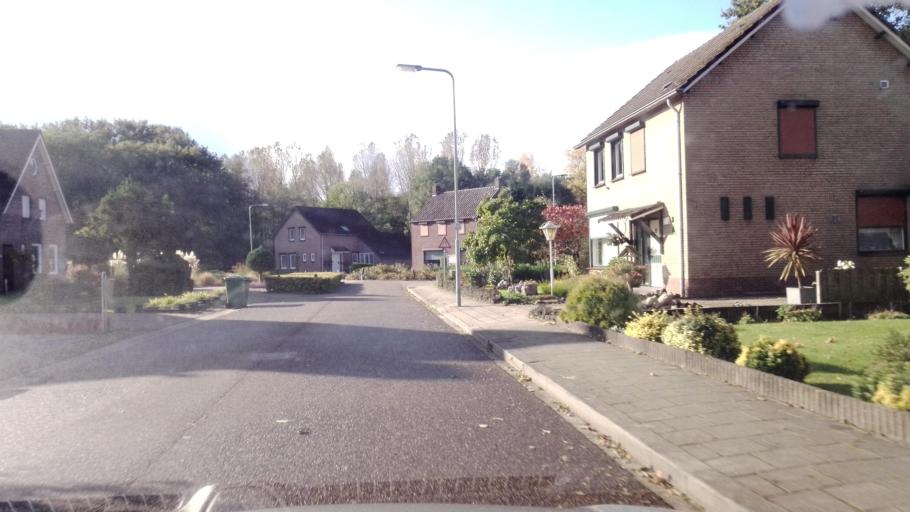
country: NL
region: Limburg
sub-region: Gemeente Venlo
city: Arcen
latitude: 51.4440
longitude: 6.1677
